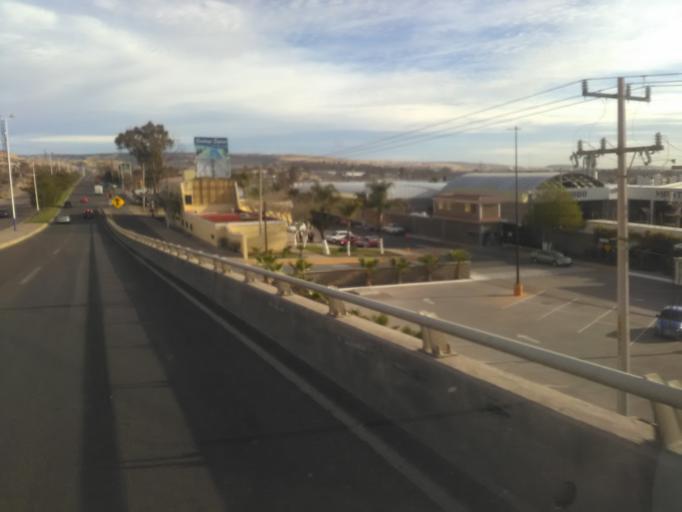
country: MX
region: Durango
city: Victoria de Durango
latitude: 24.0534
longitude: -104.6573
